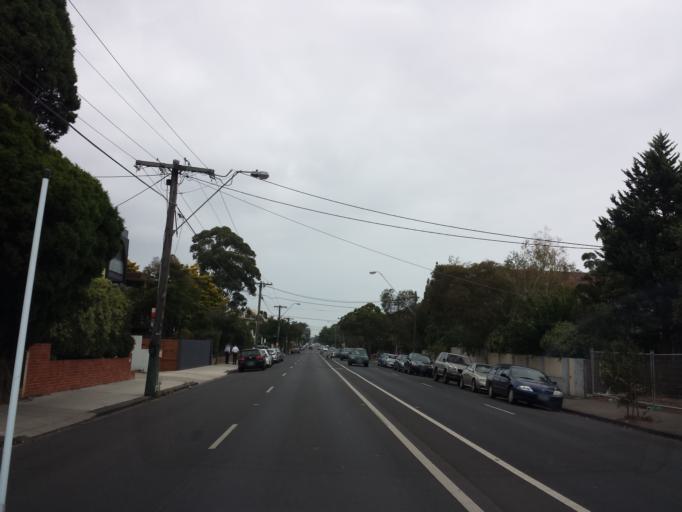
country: AU
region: Victoria
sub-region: Port Phillip
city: Balaclava
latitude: -37.8719
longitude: 144.9990
